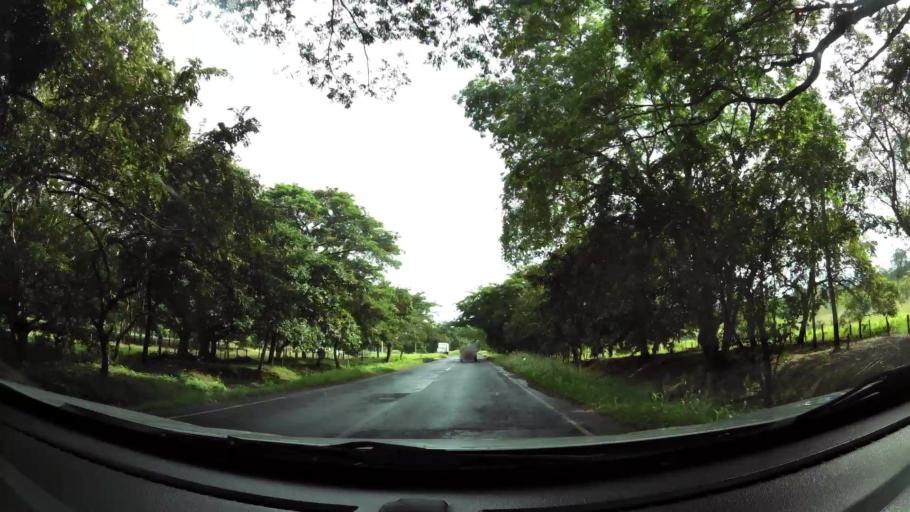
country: CR
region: Guanacaste
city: Juntas
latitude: 10.2266
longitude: -84.9780
